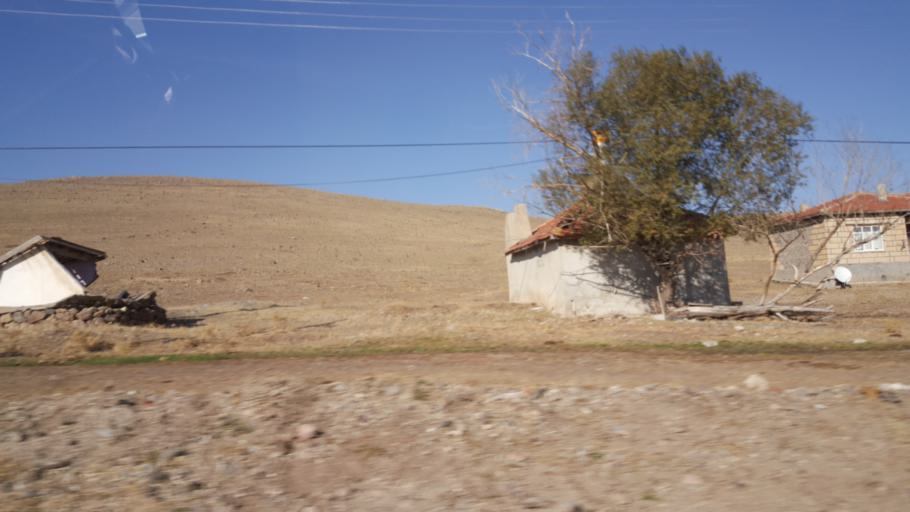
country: TR
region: Ankara
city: Altpinar
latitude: 39.1705
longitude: 32.6993
